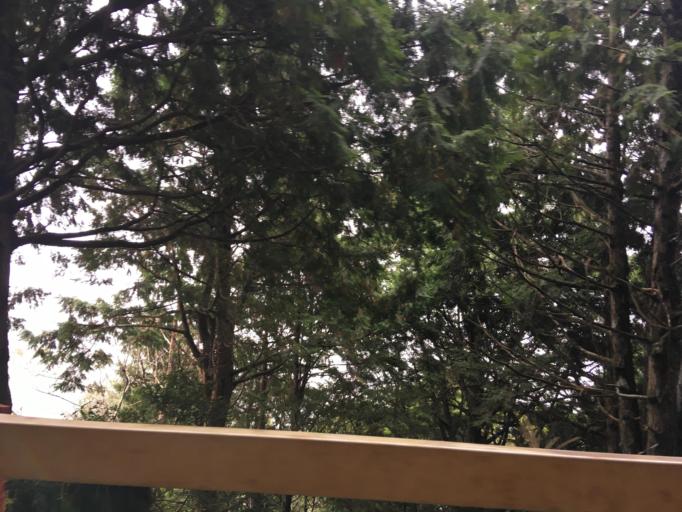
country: TW
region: Taiwan
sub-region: Yilan
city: Yilan
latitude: 24.4897
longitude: 121.5340
